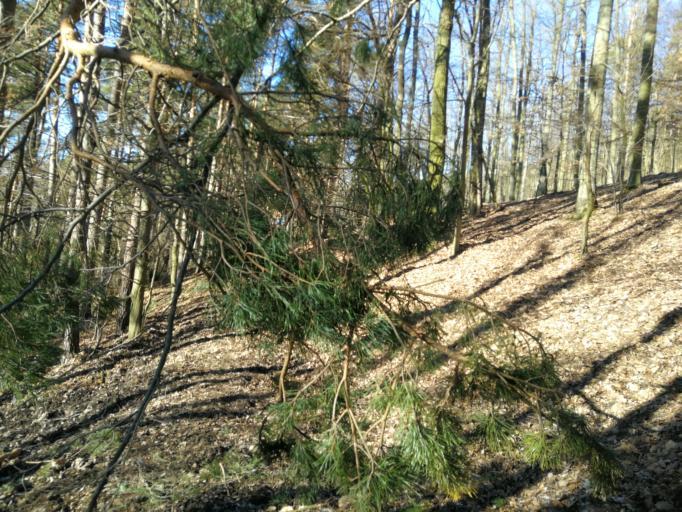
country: PL
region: Kujawsko-Pomorskie
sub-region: Powiat brodnicki
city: Gorzno
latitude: 53.2163
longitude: 19.6682
